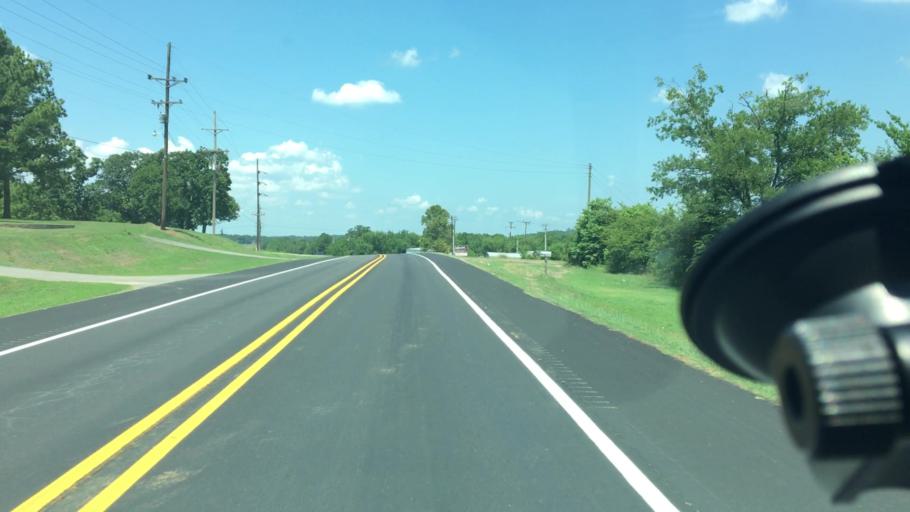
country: US
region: Arkansas
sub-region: Sebastian County
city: Lavaca
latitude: 35.3037
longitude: -94.1676
